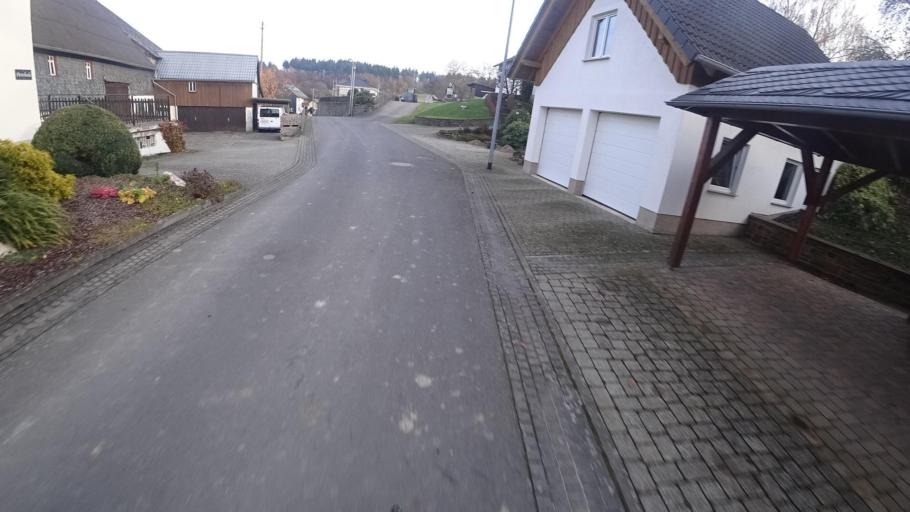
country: DE
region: Rheinland-Pfalz
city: Utzenhain
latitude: 50.1314
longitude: 7.6410
